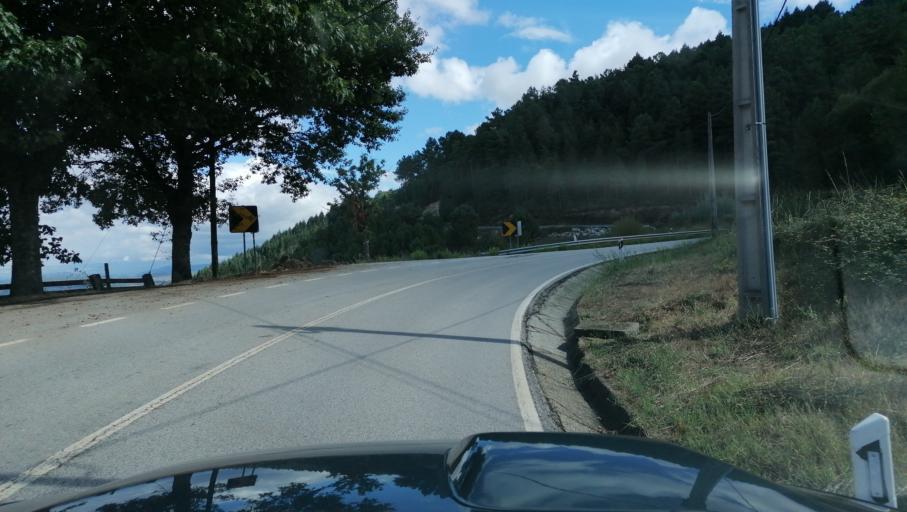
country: PT
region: Vila Real
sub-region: Vila Pouca de Aguiar
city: Vila Pouca de Aguiar
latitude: 41.5033
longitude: -7.6353
